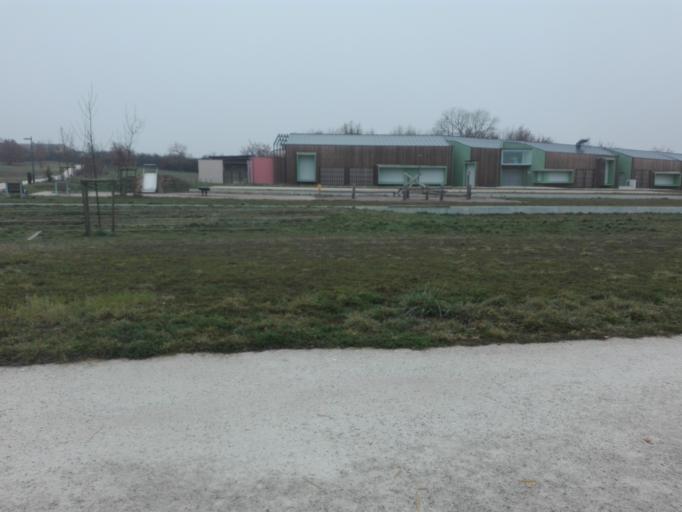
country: FR
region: Midi-Pyrenees
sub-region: Departement de la Haute-Garonne
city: Grenade
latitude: 43.7622
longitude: 1.2966
